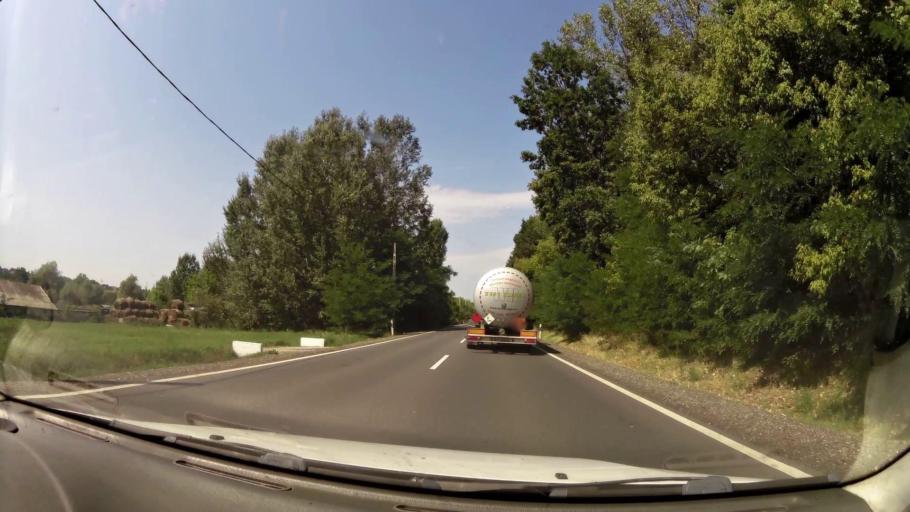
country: HU
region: Pest
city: Gyomro
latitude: 47.4377
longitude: 19.4071
